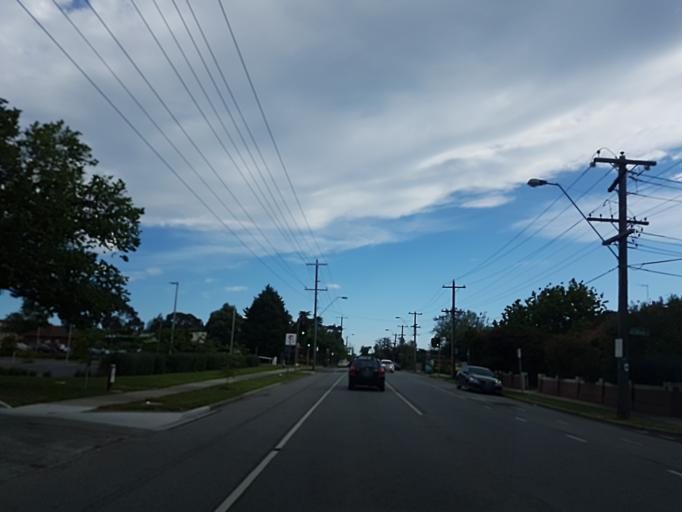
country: AU
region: Victoria
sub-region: Glen Eira
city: Caulfield
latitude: -37.8812
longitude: 145.0159
